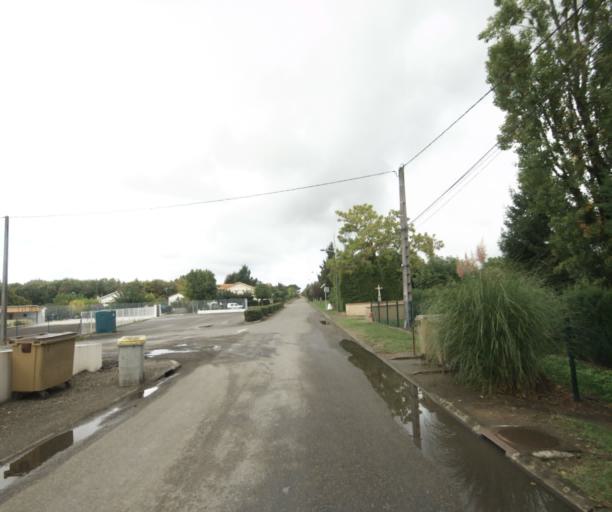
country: FR
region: Midi-Pyrenees
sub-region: Departement du Gers
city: Nogaro
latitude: 43.8177
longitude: -0.0827
